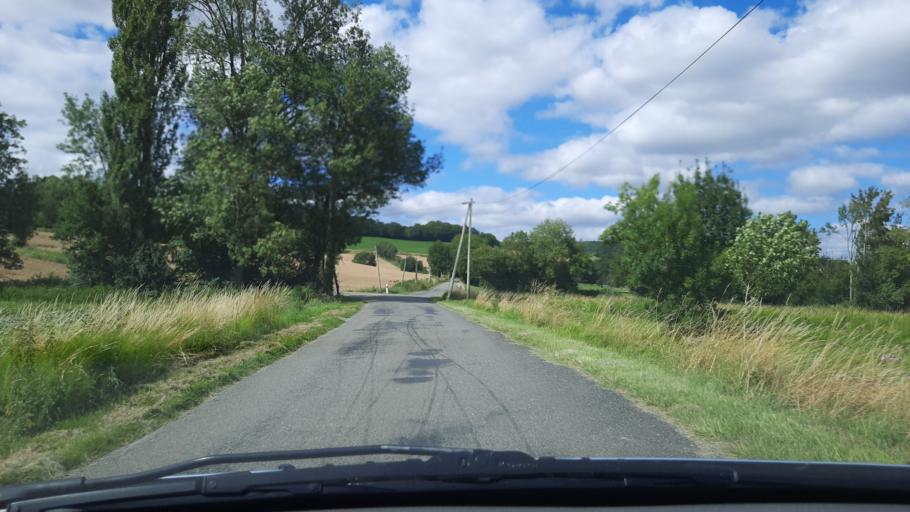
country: FR
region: Midi-Pyrenees
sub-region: Departement du Lot
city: Castelnau-Montratier
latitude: 44.2595
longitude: 1.3624
